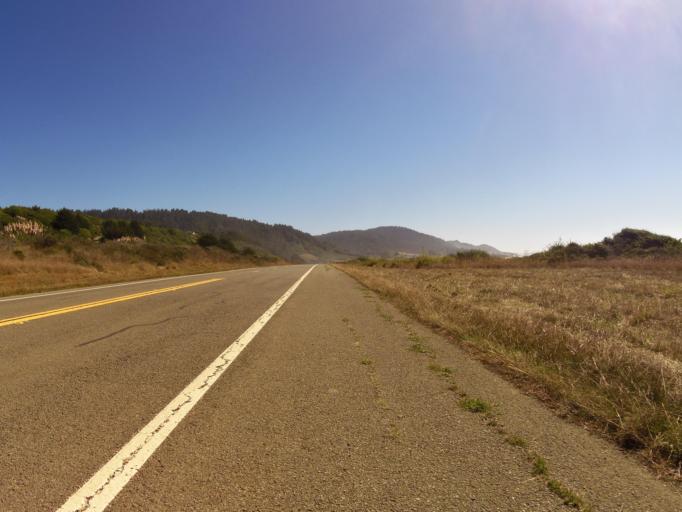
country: US
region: California
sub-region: Mendocino County
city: Fort Bragg
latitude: 39.6673
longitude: -123.7895
